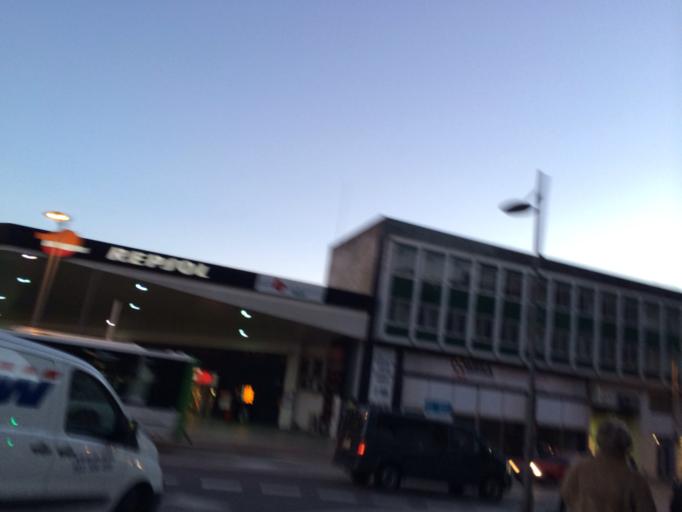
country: ES
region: Catalonia
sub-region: Provincia de Barcelona
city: les Corts
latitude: 41.3678
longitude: 2.1300
